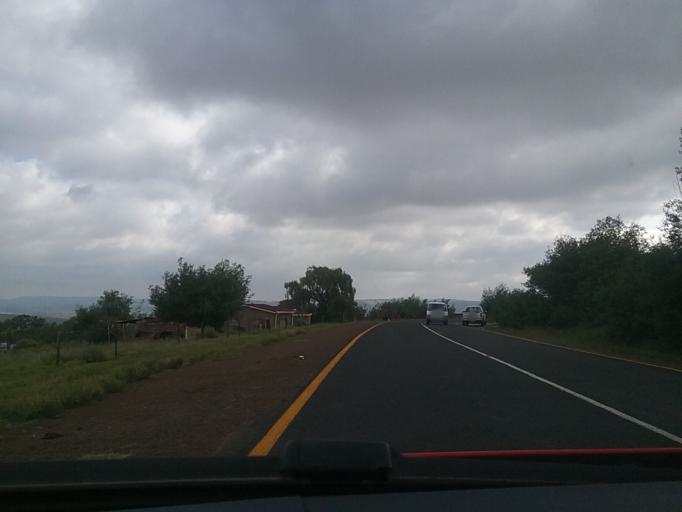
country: LS
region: Berea
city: Teyateyaneng
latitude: -29.1812
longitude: 27.7950
